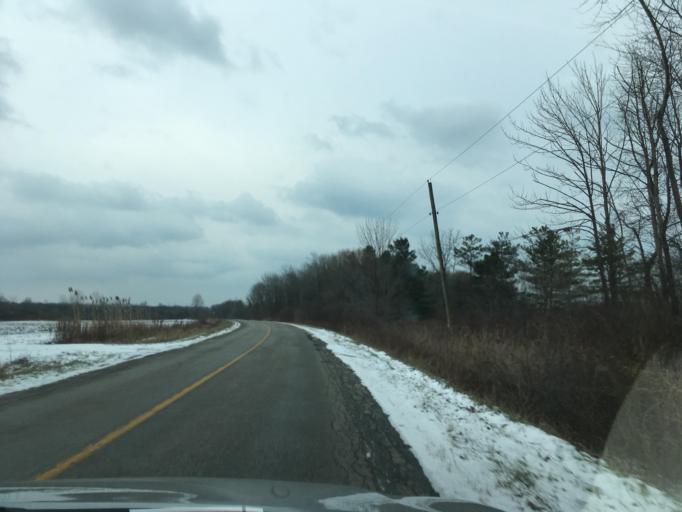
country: CA
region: Ontario
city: Norfolk County
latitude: 42.7905
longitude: -80.1146
